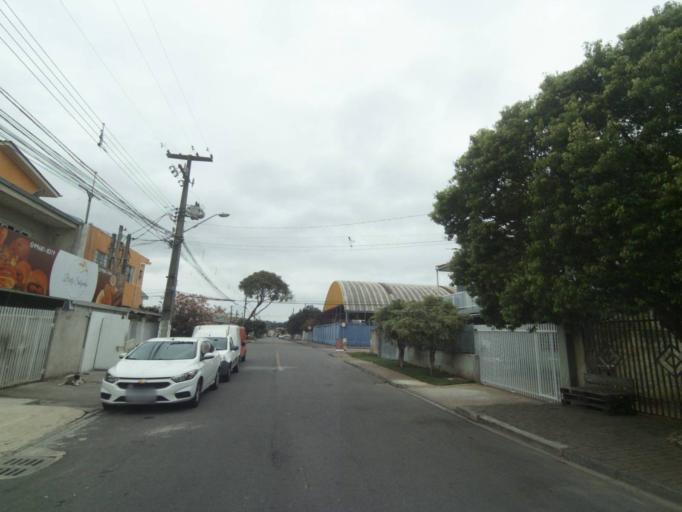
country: BR
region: Parana
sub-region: Sao Jose Dos Pinhais
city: Sao Jose dos Pinhais
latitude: -25.5364
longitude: -49.2542
